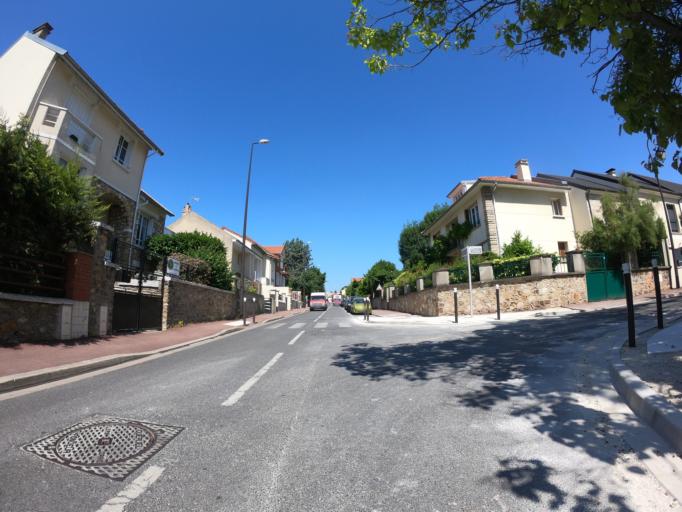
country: FR
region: Ile-de-France
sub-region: Departement des Hauts-de-Seine
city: Antony
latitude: 48.7505
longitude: 2.2913
